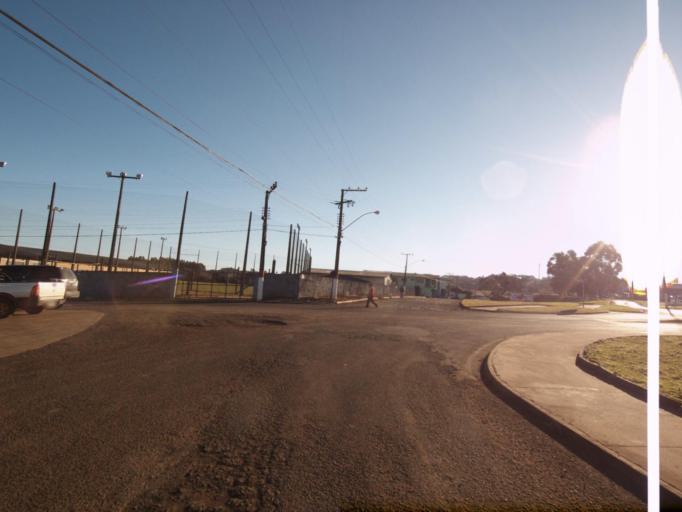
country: BR
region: Santa Catarina
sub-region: Chapeco
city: Chapeco
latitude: -26.9056
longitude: -52.9032
